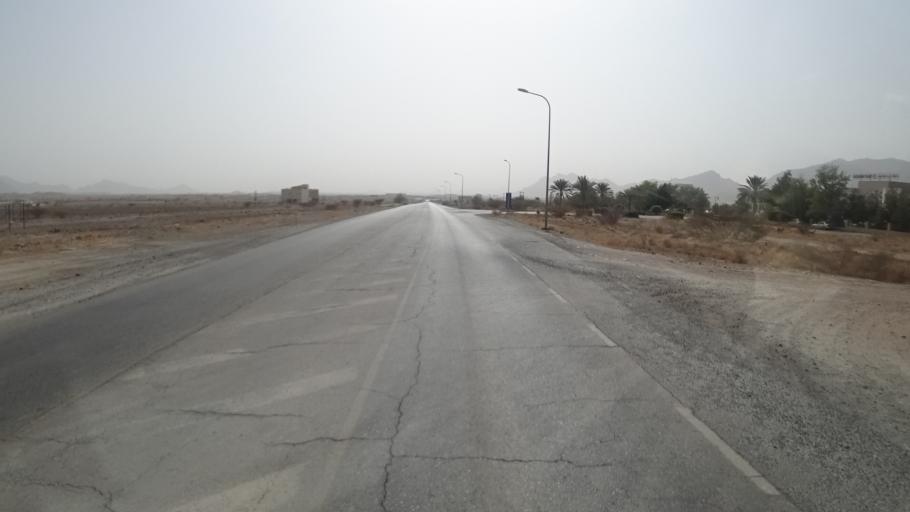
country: OM
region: Muhafazat ad Dakhiliyah
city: Nizwa
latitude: 22.9239
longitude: 57.6203
